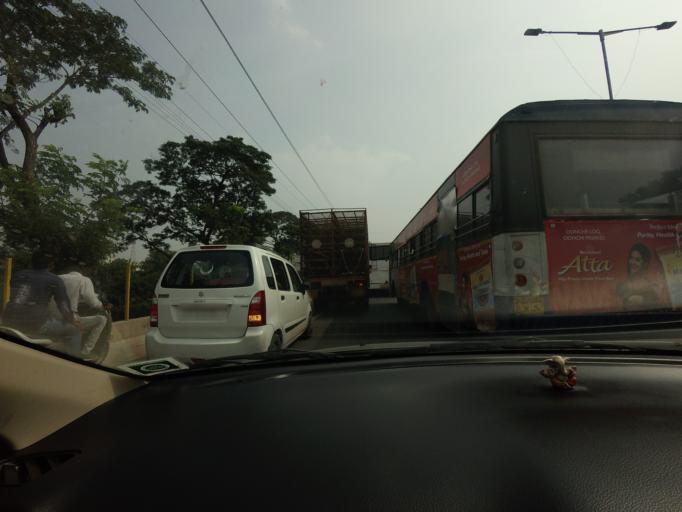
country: IN
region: Andhra Pradesh
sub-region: Krishna
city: Vijayawada
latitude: 16.4970
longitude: 80.6420
